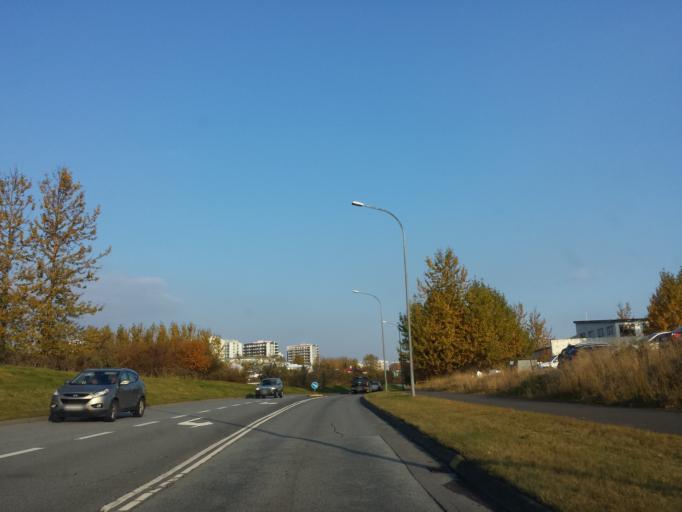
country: IS
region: Capital Region
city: Reykjavik
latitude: 64.1064
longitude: -21.8687
